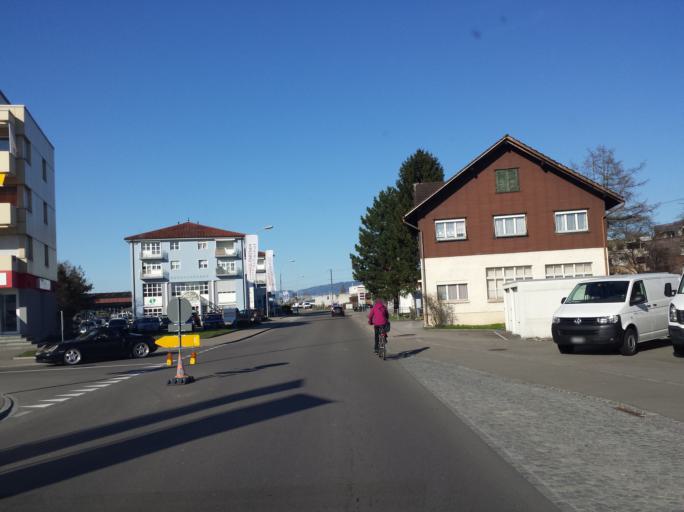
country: CH
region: Saint Gallen
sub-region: Wahlkreis Rheintal
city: Au
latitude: 47.4143
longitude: 9.6314
